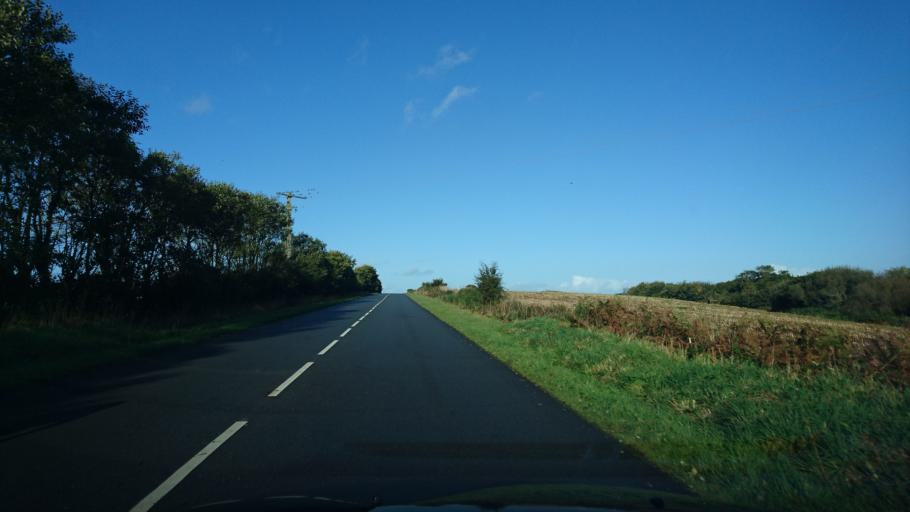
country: FR
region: Brittany
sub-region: Departement du Finistere
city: Plouarzel
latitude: 48.4387
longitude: -4.7325
